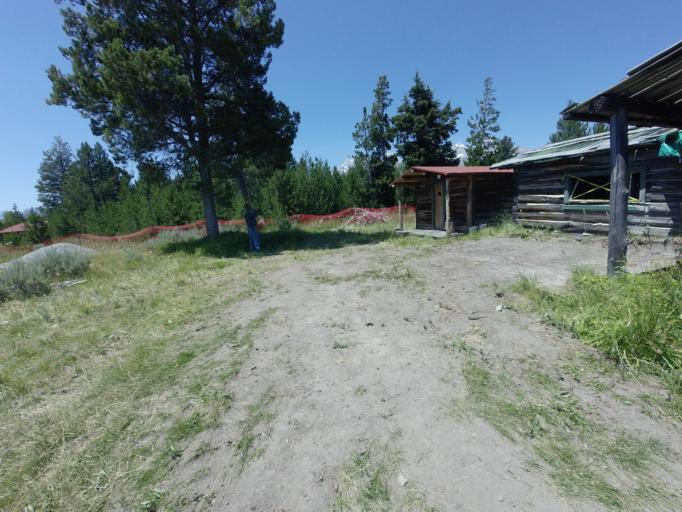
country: US
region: Wyoming
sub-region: Teton County
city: Jackson
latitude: 43.6949
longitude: -110.6956
